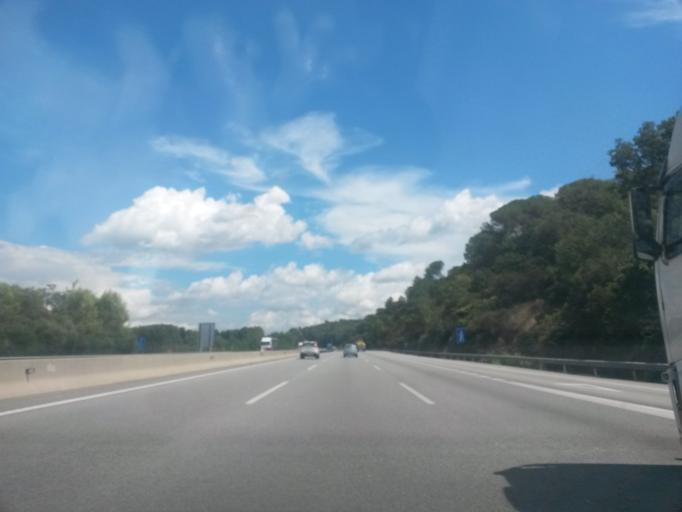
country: ES
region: Catalonia
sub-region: Provincia de Girona
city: Breda
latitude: 41.7258
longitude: 2.5937
